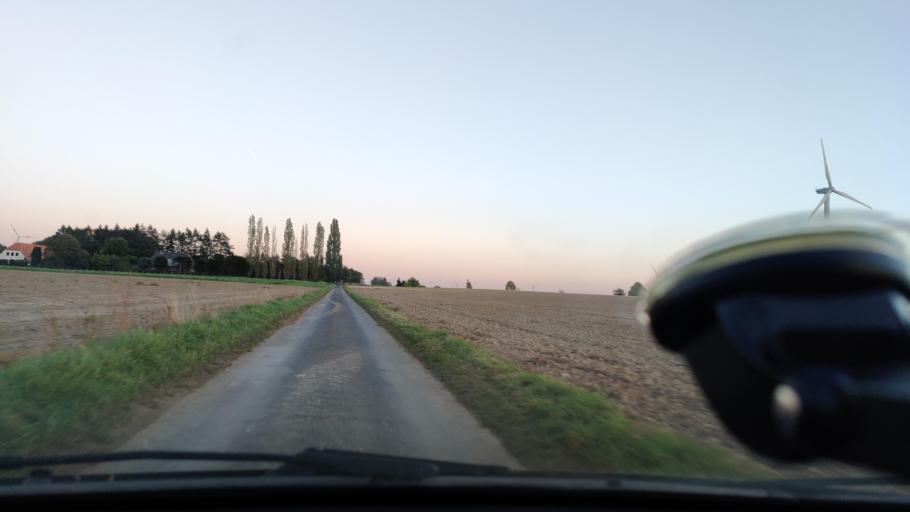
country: DE
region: North Rhine-Westphalia
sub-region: Regierungsbezirk Dusseldorf
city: Goch
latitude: 51.7144
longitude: 6.1968
